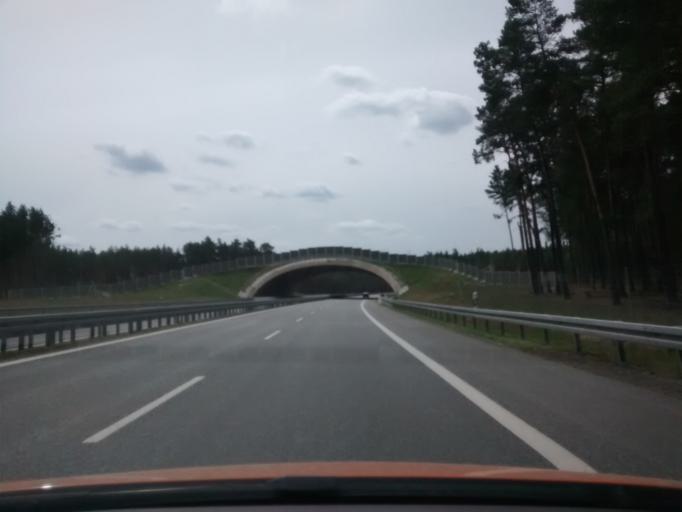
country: DE
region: Brandenburg
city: Trebbin
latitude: 52.1560
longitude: 13.2403
